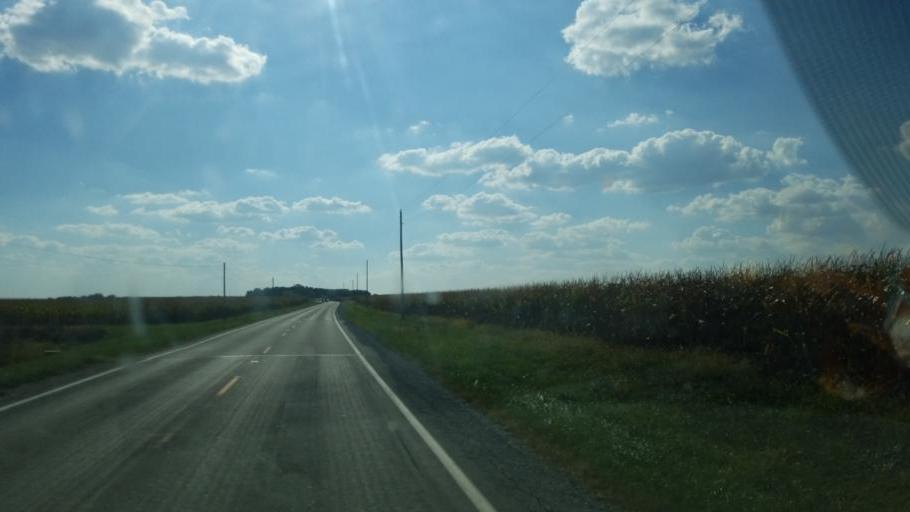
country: US
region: Ohio
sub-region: Wyandot County
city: Upper Sandusky
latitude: 40.7469
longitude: -83.3596
